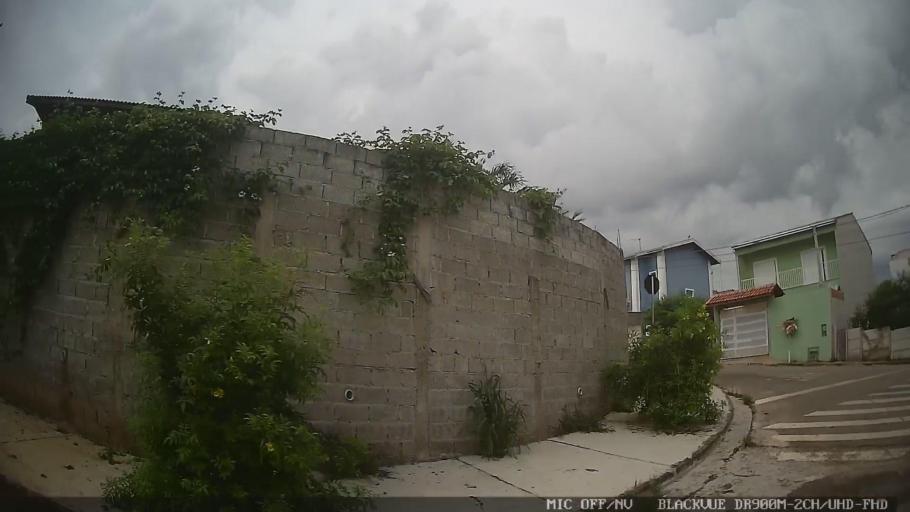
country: BR
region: Sao Paulo
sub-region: Atibaia
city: Atibaia
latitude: -23.1240
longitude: -46.5889
